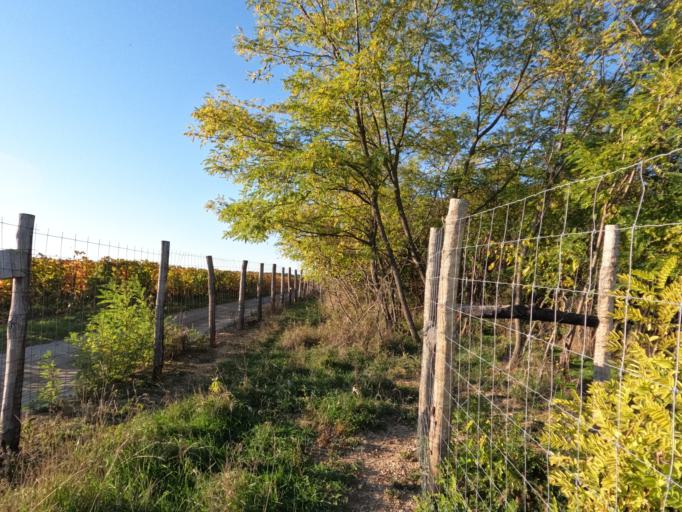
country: HU
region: Tolna
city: Szekszard
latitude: 46.3081
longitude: 18.6598
